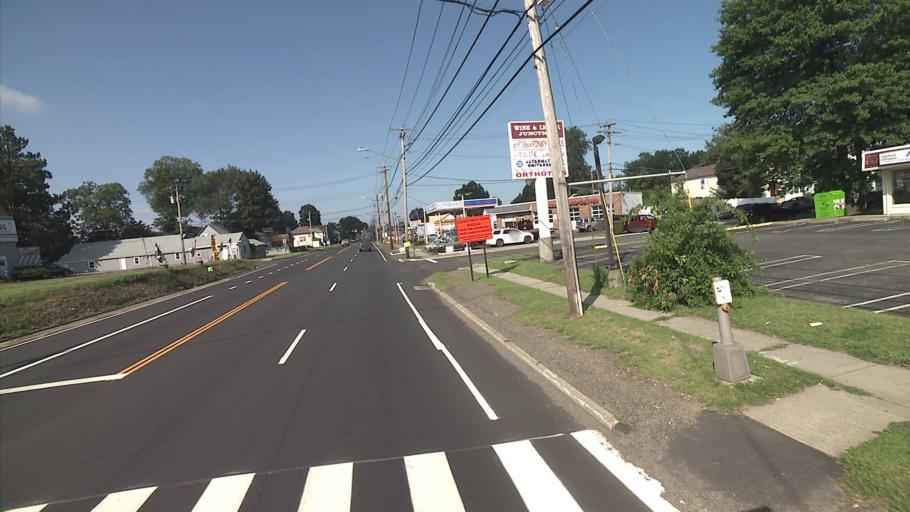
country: US
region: Connecticut
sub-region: New Haven County
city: City of Milford (balance)
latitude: 41.2049
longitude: -73.0947
